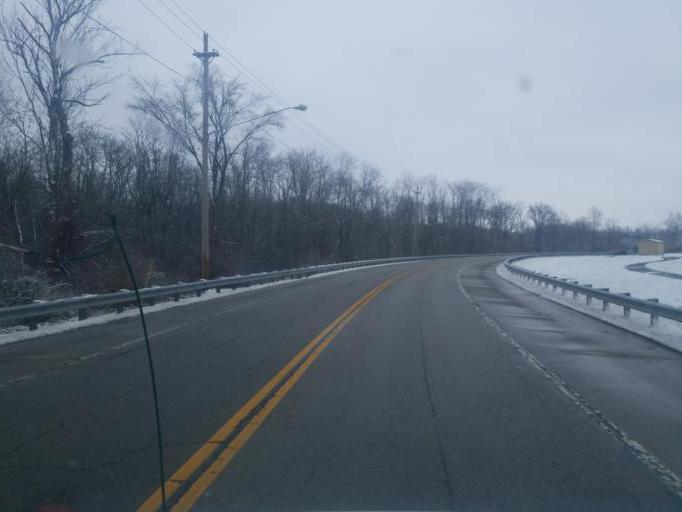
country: US
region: Ohio
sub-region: Geauga County
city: Middlefield
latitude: 41.4682
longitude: -81.0865
